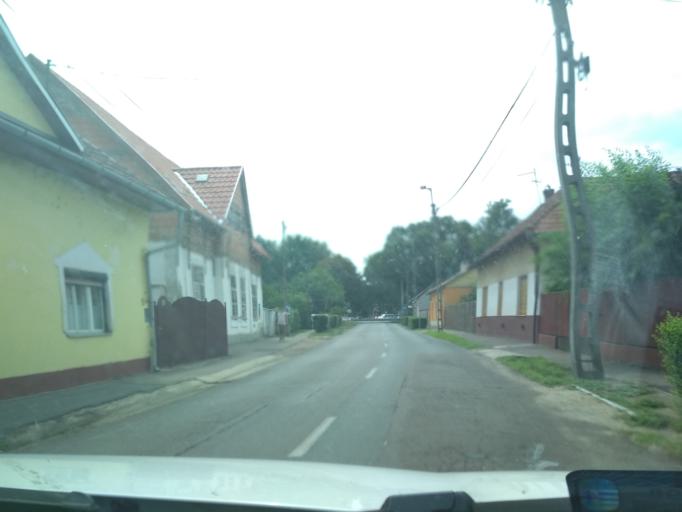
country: HU
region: Jasz-Nagykun-Szolnok
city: Tiszafured
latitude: 47.6227
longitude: 20.7546
